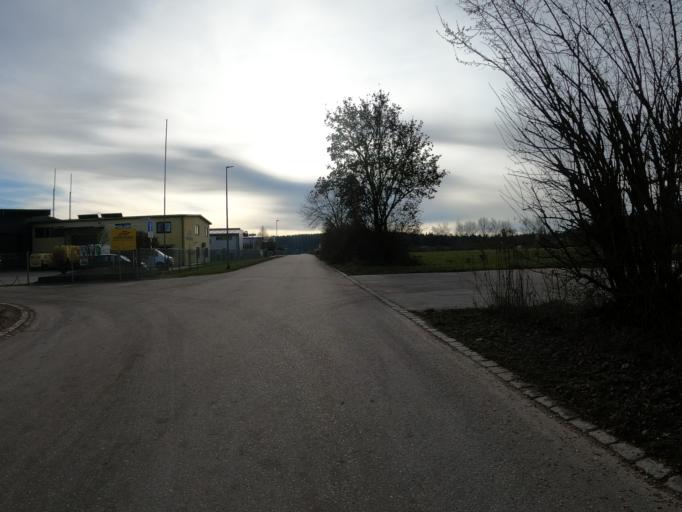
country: DE
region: Bavaria
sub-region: Swabia
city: Nersingen
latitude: 48.4200
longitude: 10.1738
